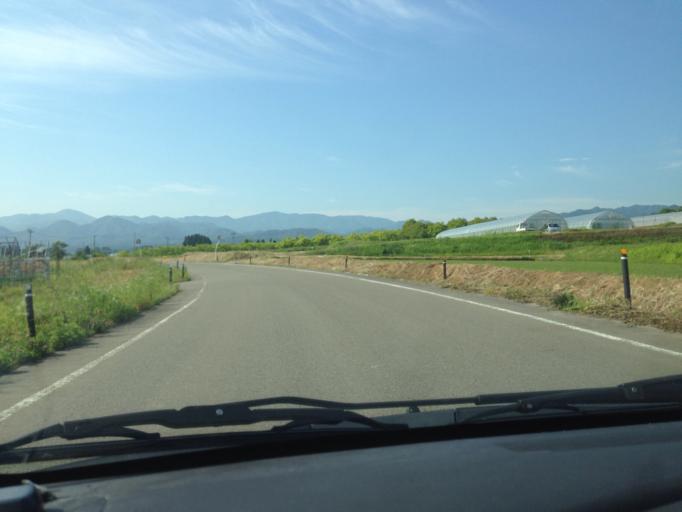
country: JP
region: Fukushima
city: Kitakata
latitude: 37.4688
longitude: 139.8131
